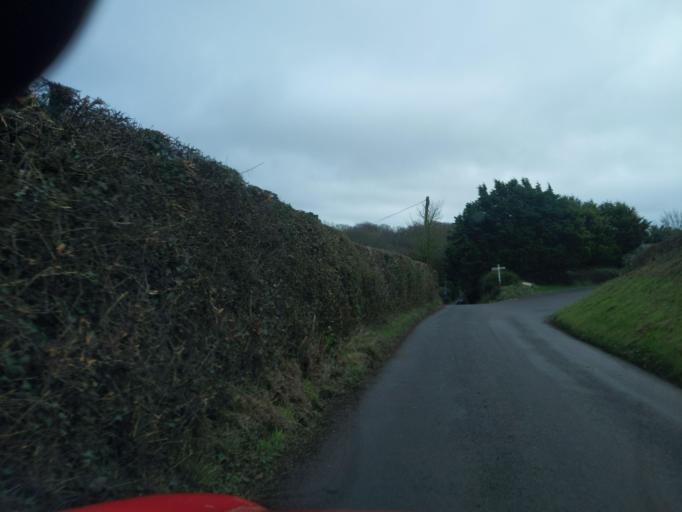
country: GB
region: England
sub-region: Devon
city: Wembury
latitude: 50.3289
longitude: -4.0919
